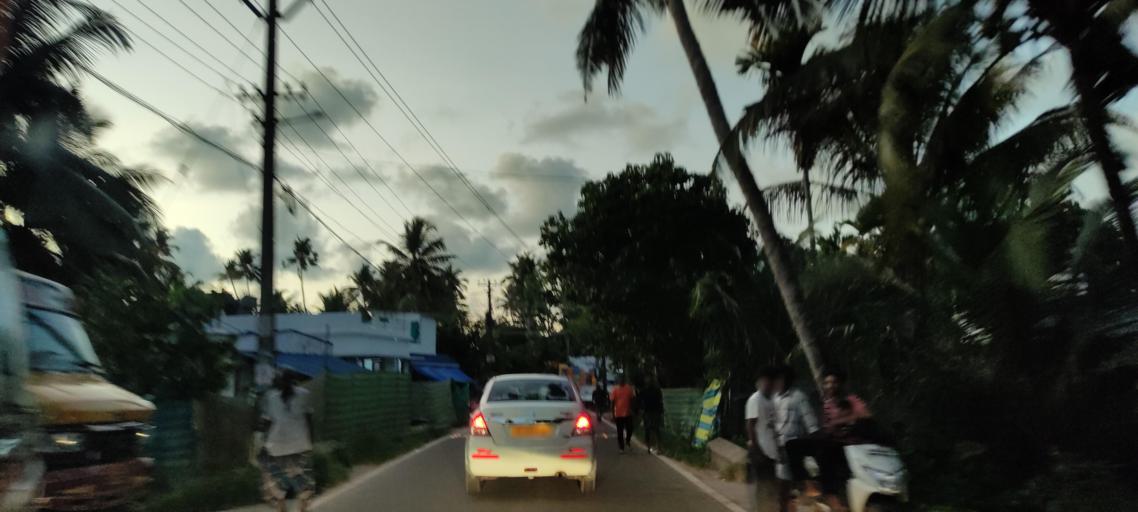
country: IN
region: Kerala
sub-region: Alappuzha
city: Kutiatodu
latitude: 9.7875
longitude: 76.2783
